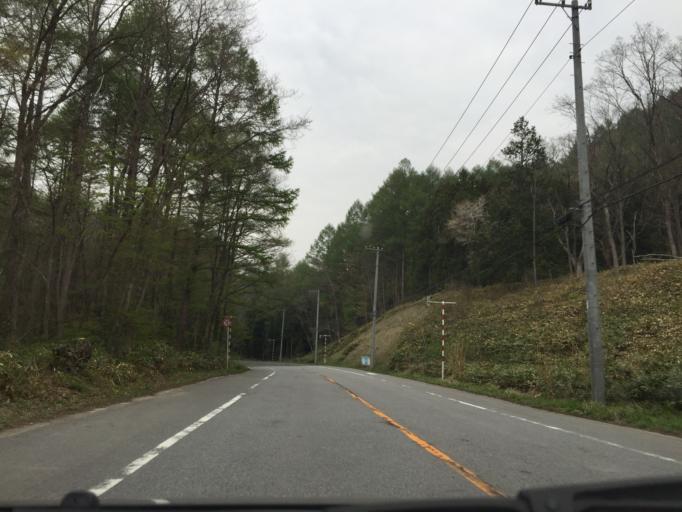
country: JP
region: Tochigi
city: Nikko
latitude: 37.0325
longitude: 139.7269
